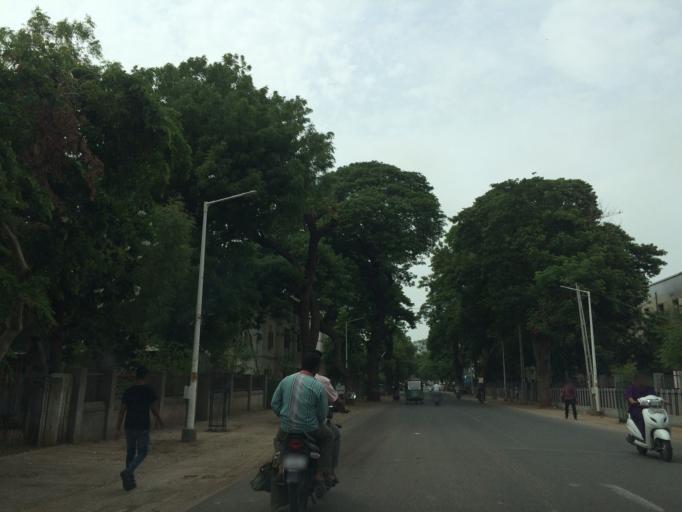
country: IN
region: Gujarat
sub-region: Anand
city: Karamsad
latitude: 22.5509
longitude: 72.9288
